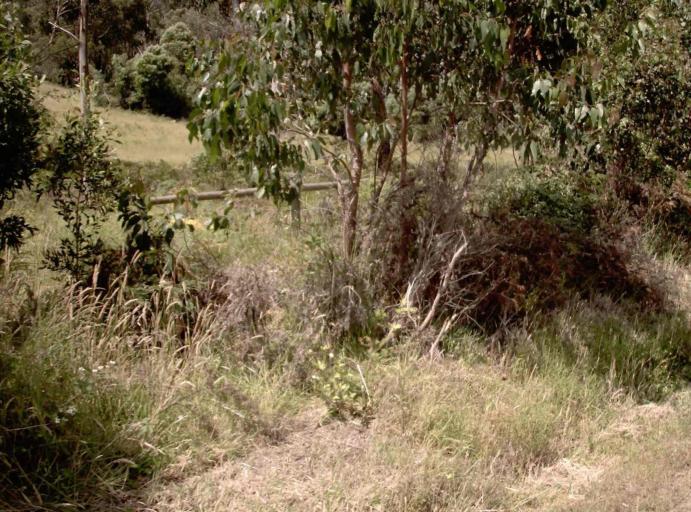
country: AU
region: Victoria
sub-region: Latrobe
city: Traralgon
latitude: -38.3068
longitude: 146.5462
